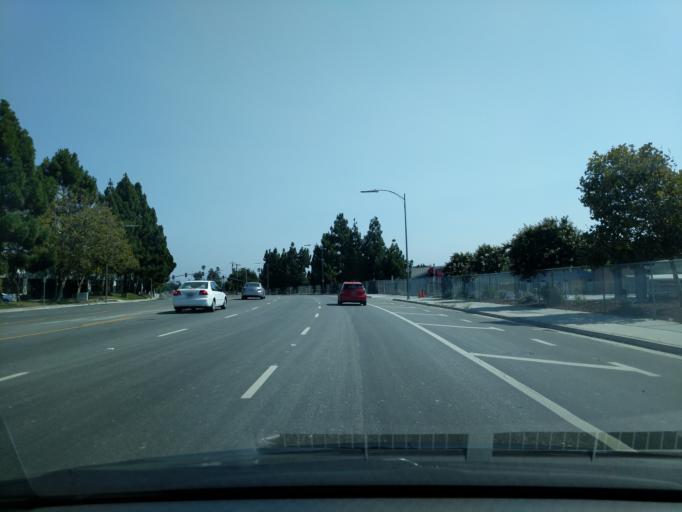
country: US
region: California
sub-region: Santa Clara County
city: Milpitas
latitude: 37.3901
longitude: -121.9009
